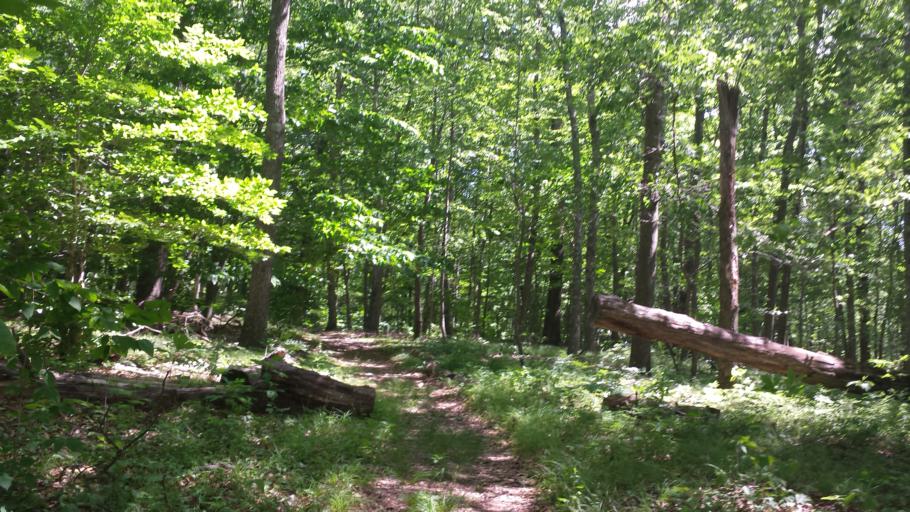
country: US
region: New York
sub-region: Westchester County
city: Pound Ridge
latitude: 41.2684
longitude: -73.5838
